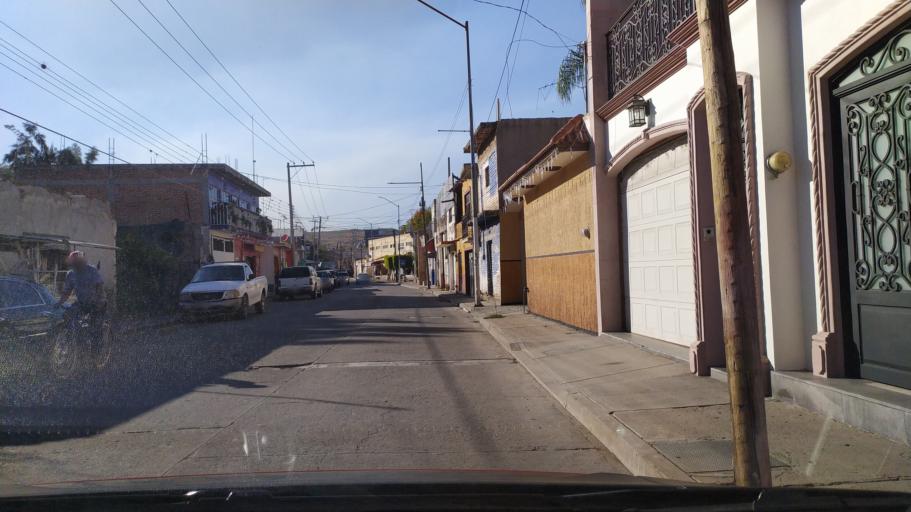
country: MX
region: Guanajuato
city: Ciudad Manuel Doblado
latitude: 20.7252
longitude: -101.9492
